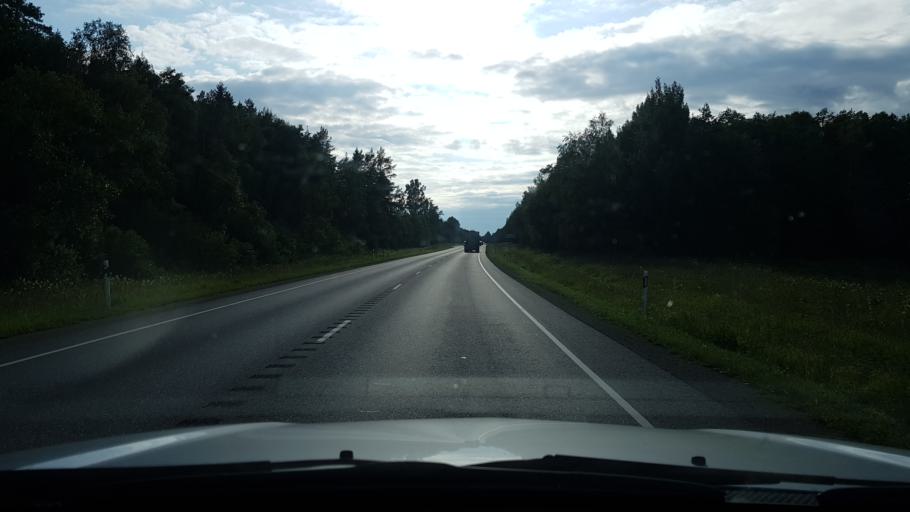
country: EE
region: Ida-Virumaa
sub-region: Toila vald
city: Voka
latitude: 59.3928
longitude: 27.6535
